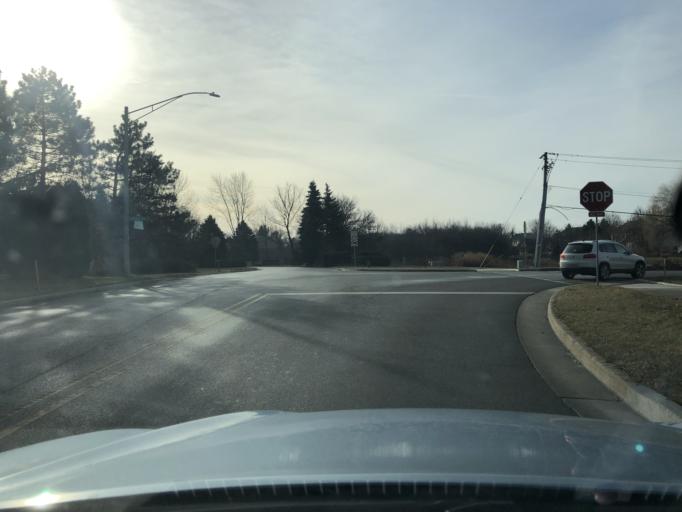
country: US
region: Illinois
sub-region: McHenry County
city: Algonquin
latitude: 42.1540
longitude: -88.3166
